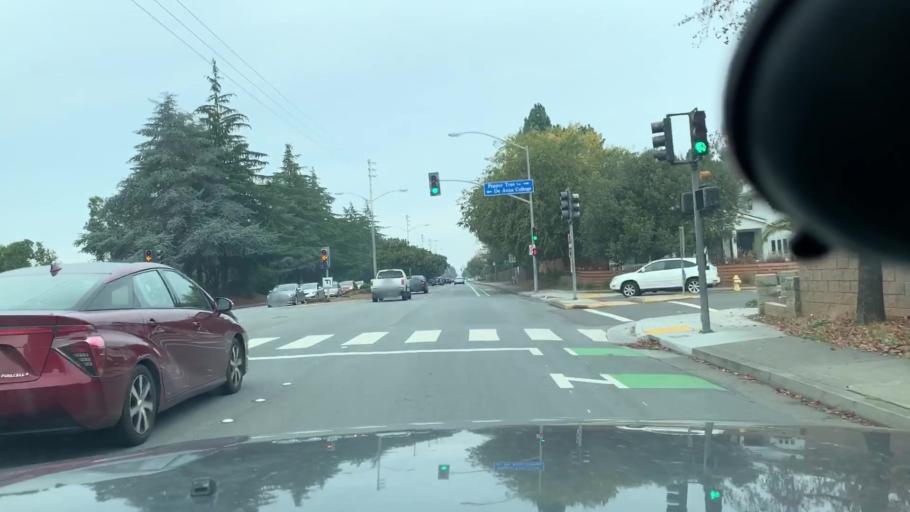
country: US
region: California
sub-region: Santa Clara County
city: Cupertino
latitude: 37.3194
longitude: -122.0414
